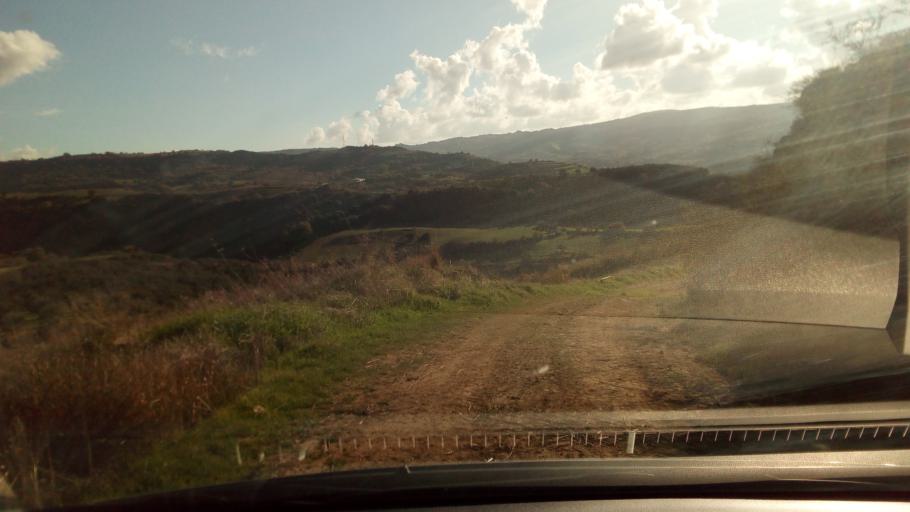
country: CY
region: Pafos
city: Polis
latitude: 34.9400
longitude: 32.4898
